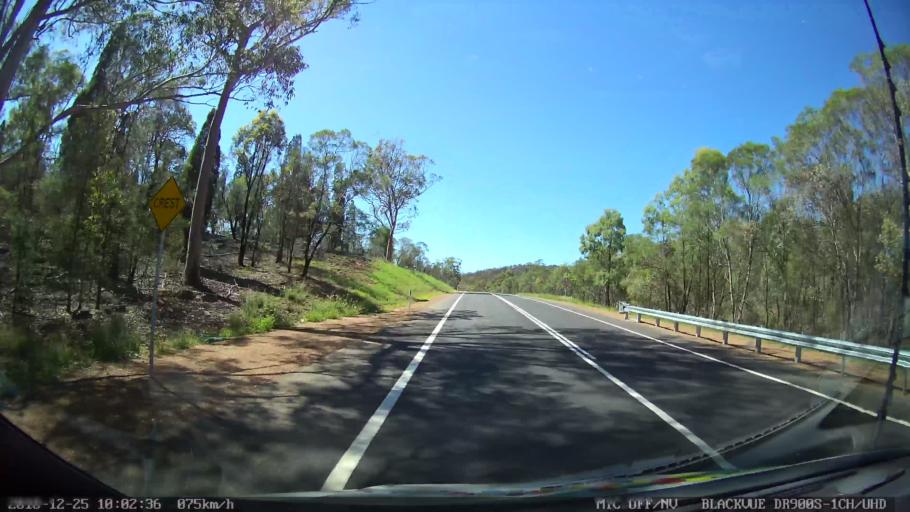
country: AU
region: New South Wales
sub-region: Upper Hunter Shire
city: Merriwa
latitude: -32.2202
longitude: 150.4644
